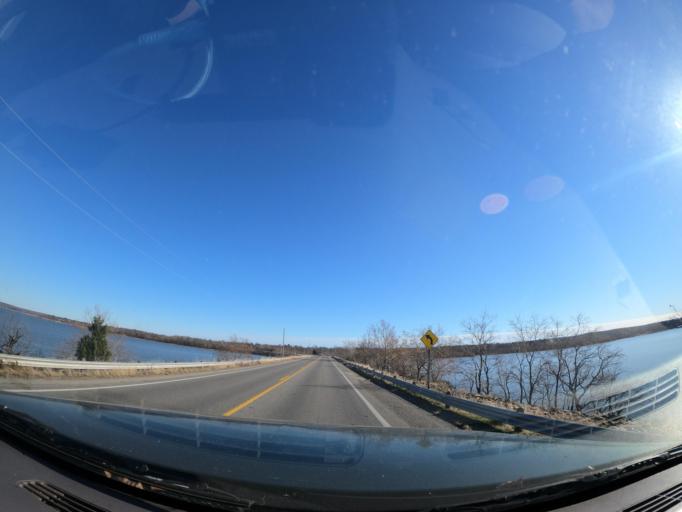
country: US
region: Oklahoma
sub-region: Pittsburg County
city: Longtown
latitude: 35.2421
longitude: -95.5597
